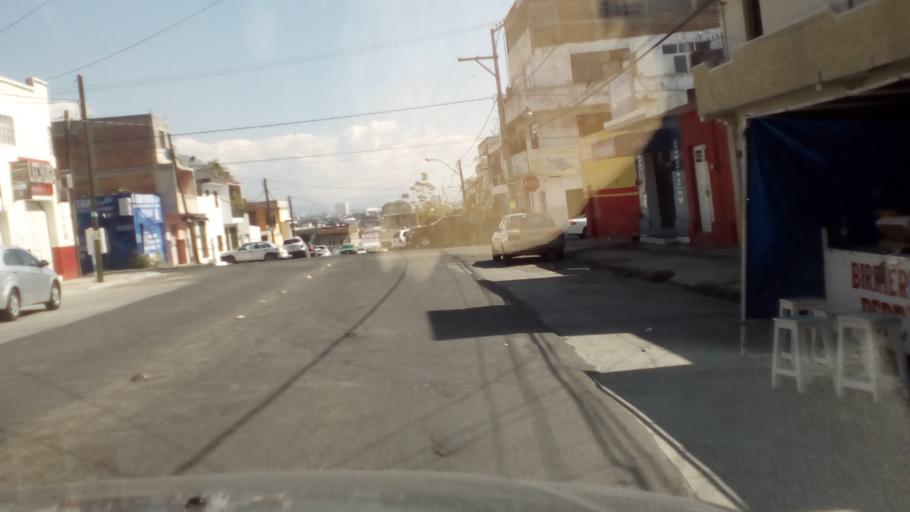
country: MX
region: Guanajuato
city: Leon
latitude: 21.1195
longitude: -101.6899
